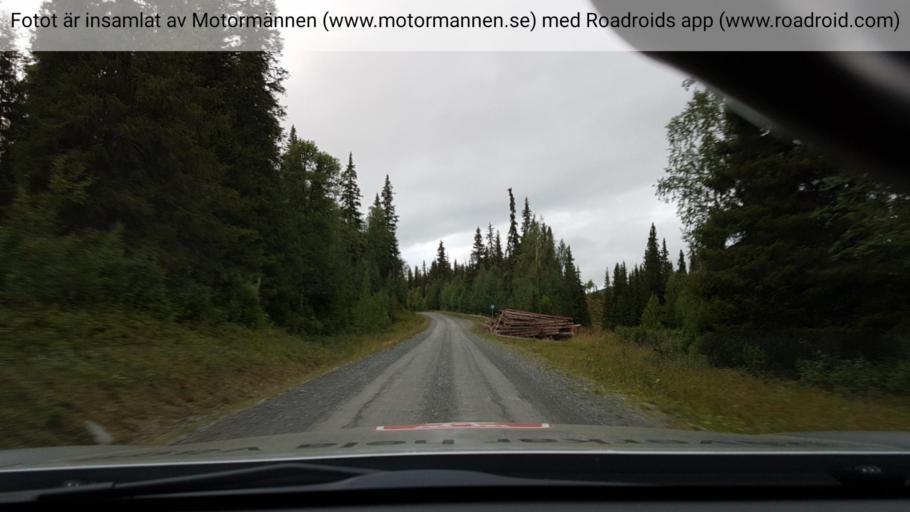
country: SE
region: Vaesterbotten
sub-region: Vilhelmina Kommun
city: Sjoberg
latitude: 65.5378
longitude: 15.4320
